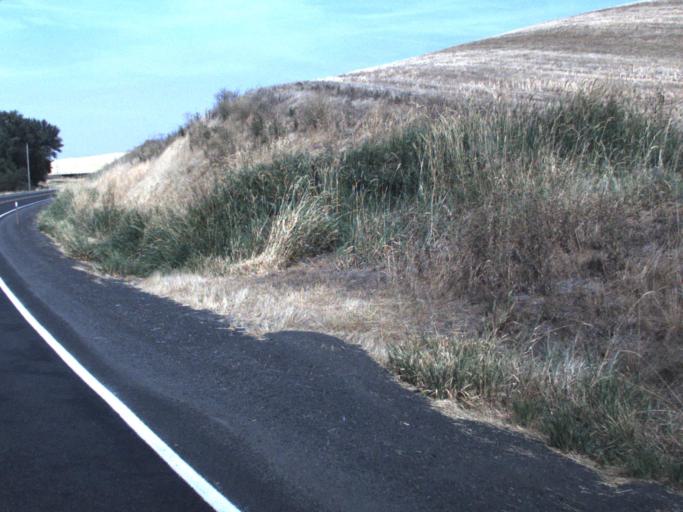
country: US
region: Washington
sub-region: Whitman County
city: Pullman
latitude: 46.9702
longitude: -117.1194
